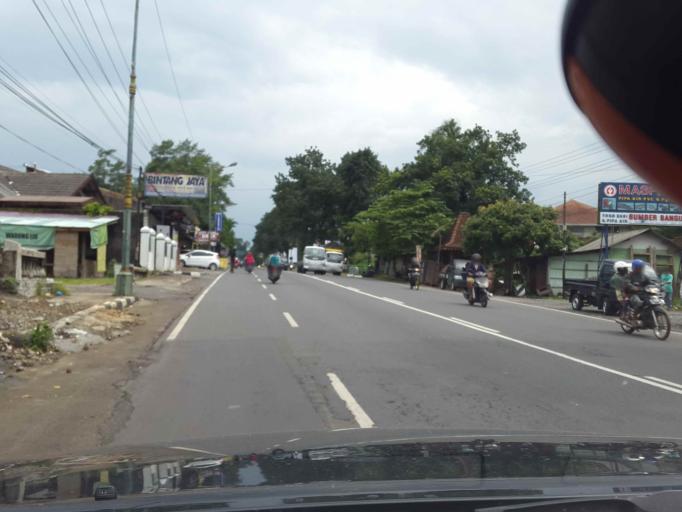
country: ID
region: Central Java
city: Salatiga
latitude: -7.3515
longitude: 110.5124
